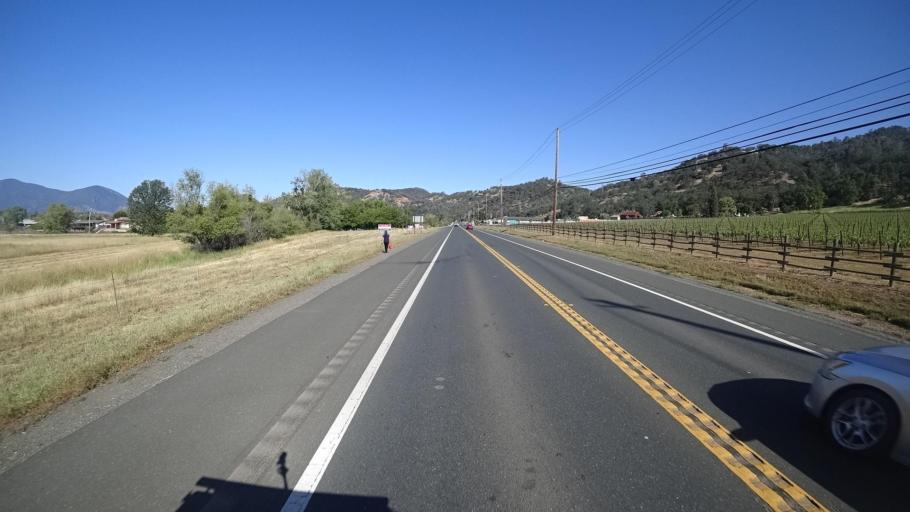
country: US
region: California
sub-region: Lake County
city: Clearlake Oaks
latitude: 39.0233
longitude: -122.6555
